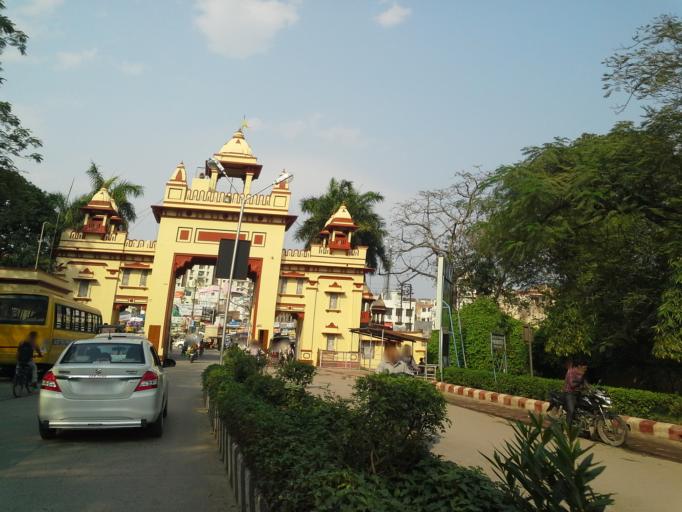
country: IN
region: Uttar Pradesh
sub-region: Varanasi
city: Ramnagar
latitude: 25.2772
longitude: 83.0018
